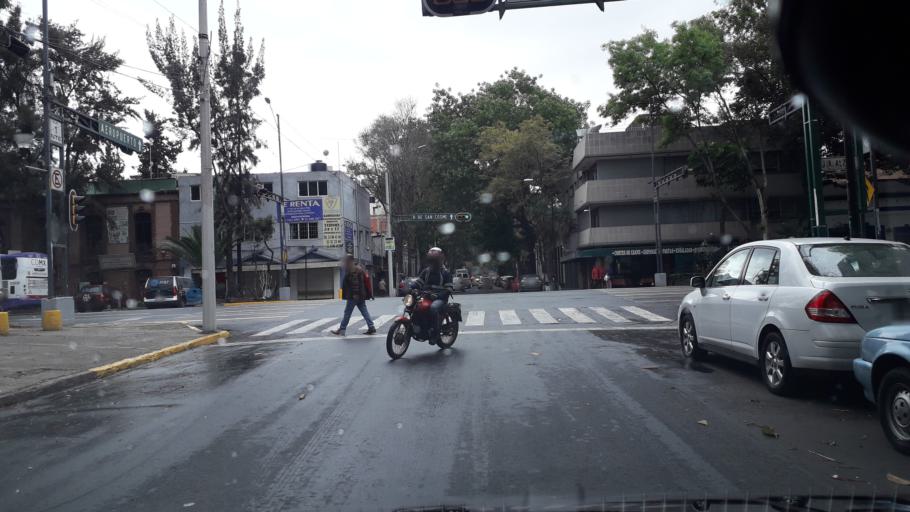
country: MX
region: Mexico City
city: Cuauhtemoc
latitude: 19.4471
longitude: -99.1566
